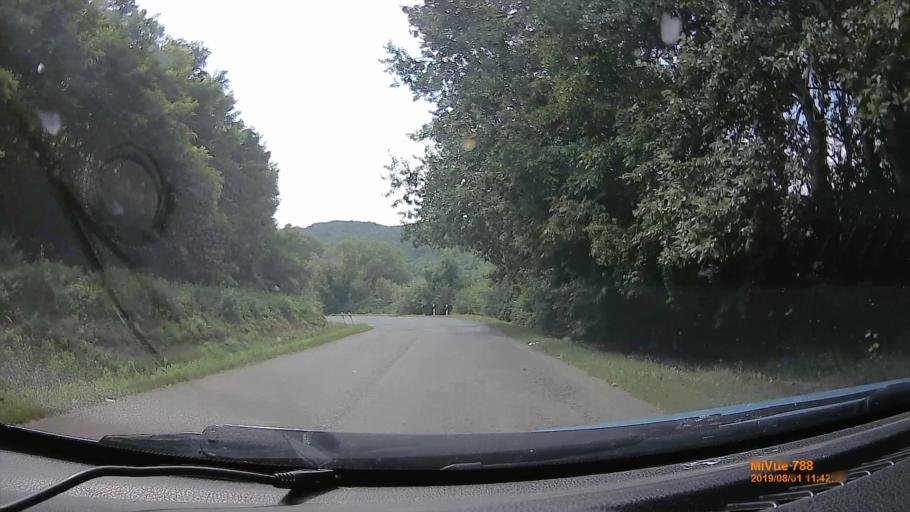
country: HU
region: Baranya
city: Villany
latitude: 45.8844
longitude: 18.4113
